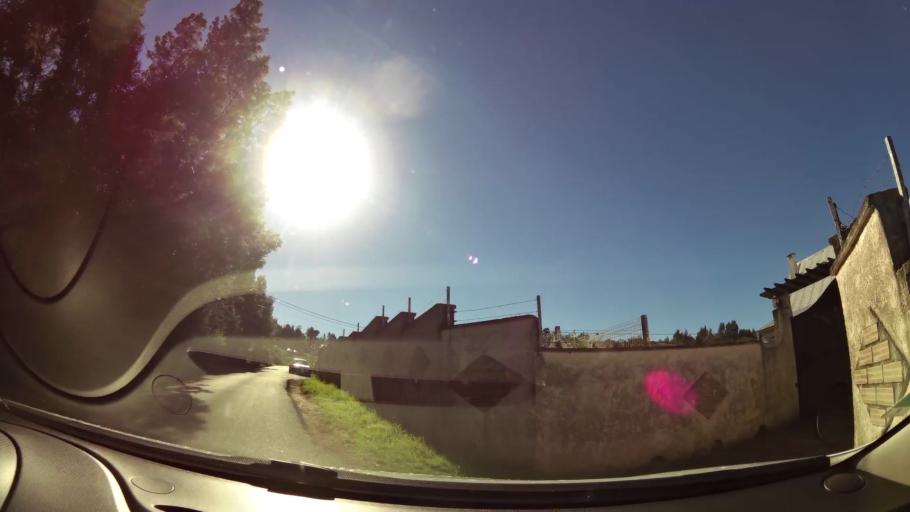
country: RE
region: Reunion
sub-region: Reunion
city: Le Tampon
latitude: -21.2313
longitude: 55.5430
